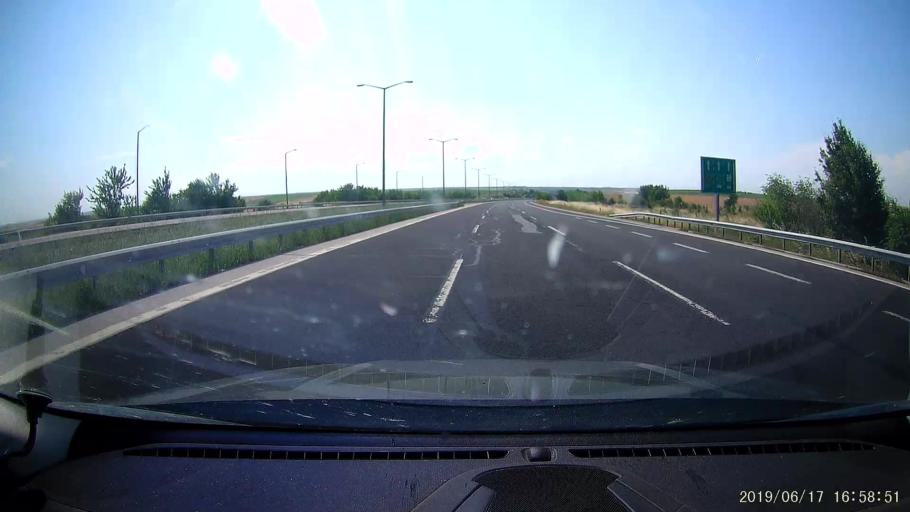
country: TR
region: Edirne
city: Haskoy
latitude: 41.6108
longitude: 26.8761
